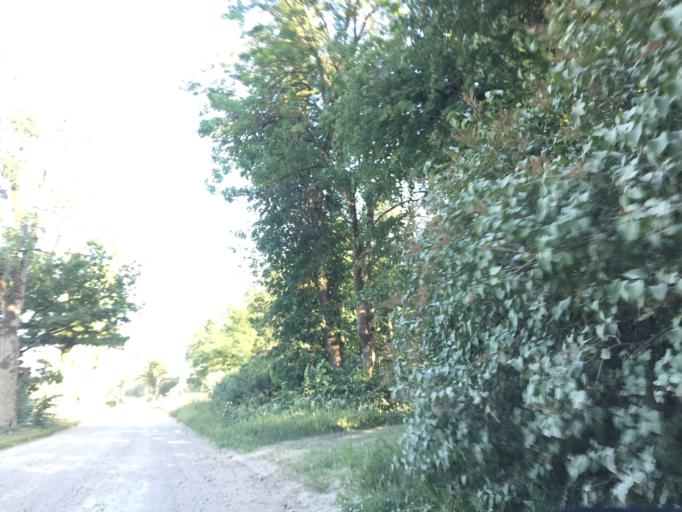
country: LV
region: Skriveri
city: Skriveri
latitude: 56.8359
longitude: 25.2132
